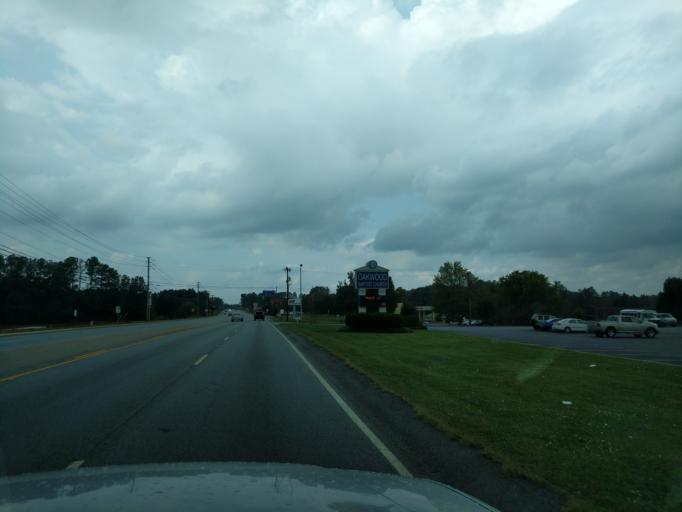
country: US
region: South Carolina
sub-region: Anderson County
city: Centerville
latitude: 34.5054
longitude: -82.6848
